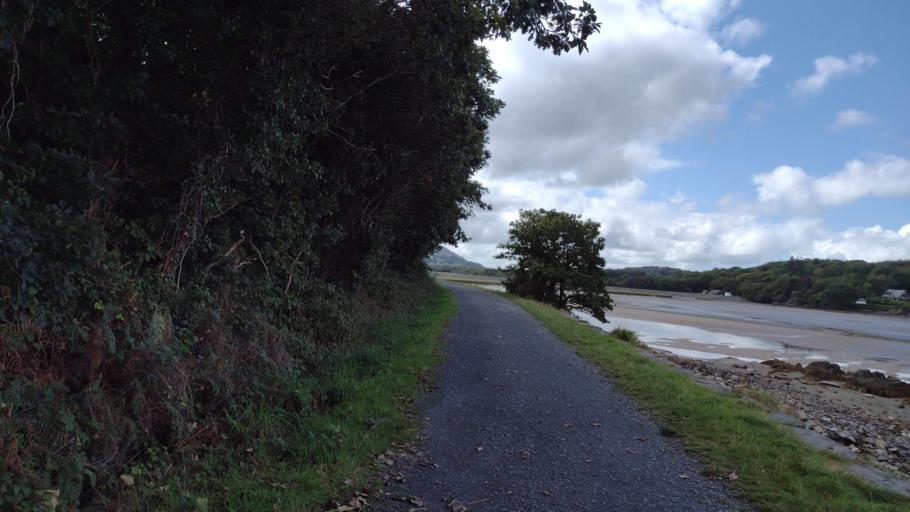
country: GB
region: Wales
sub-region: Gwynedd
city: Barmouth
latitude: 52.7209
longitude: -4.0078
